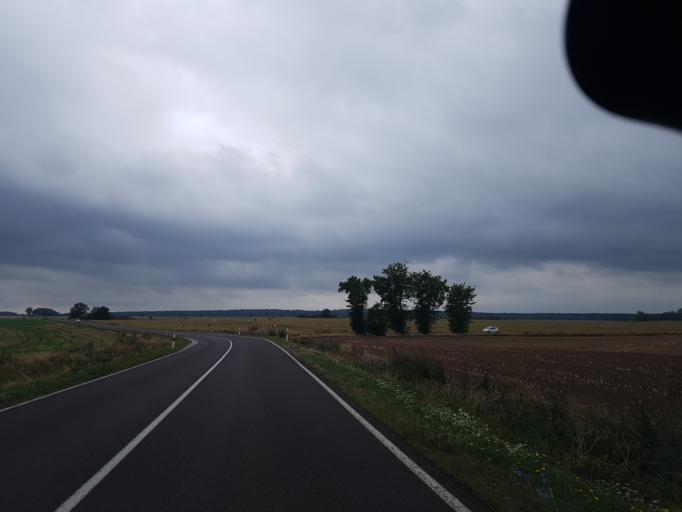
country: DE
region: Saxony-Anhalt
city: Loburg
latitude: 52.1619
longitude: 12.1099
